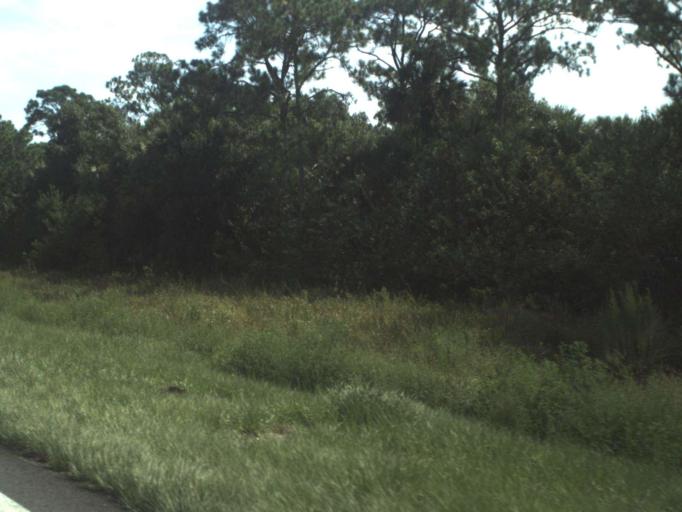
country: US
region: Florida
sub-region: Indian River County
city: Fellsmere
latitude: 27.7592
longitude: -80.5514
